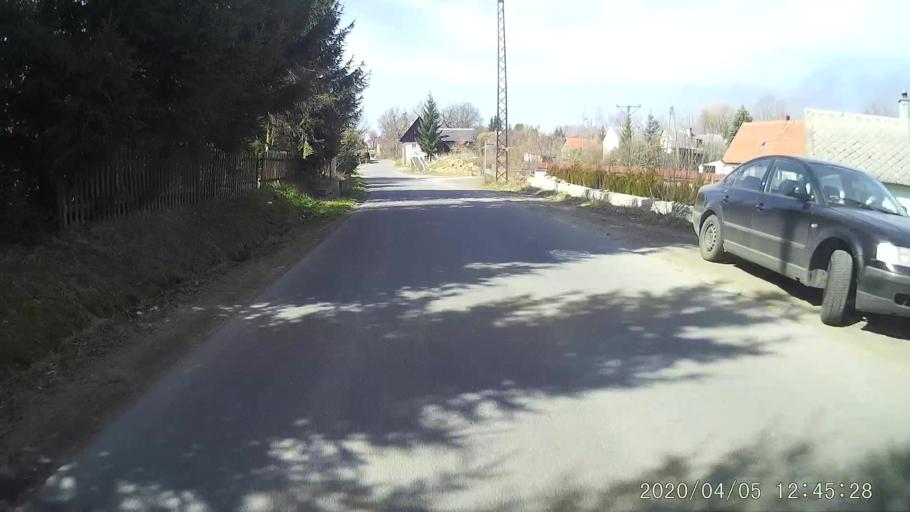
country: PL
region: Lower Silesian Voivodeship
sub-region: Powiat lwowecki
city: Mirsk
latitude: 50.9773
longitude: 15.3536
